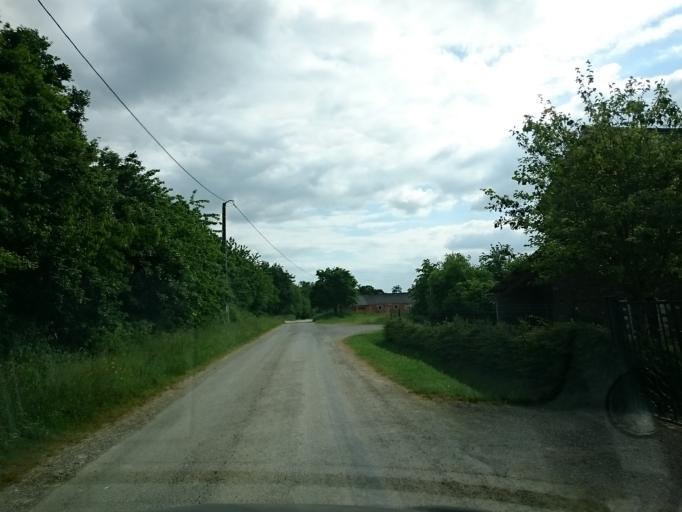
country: FR
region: Brittany
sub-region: Departement d'Ille-et-Vilaine
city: Crevin
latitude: 47.9548
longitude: -1.6891
